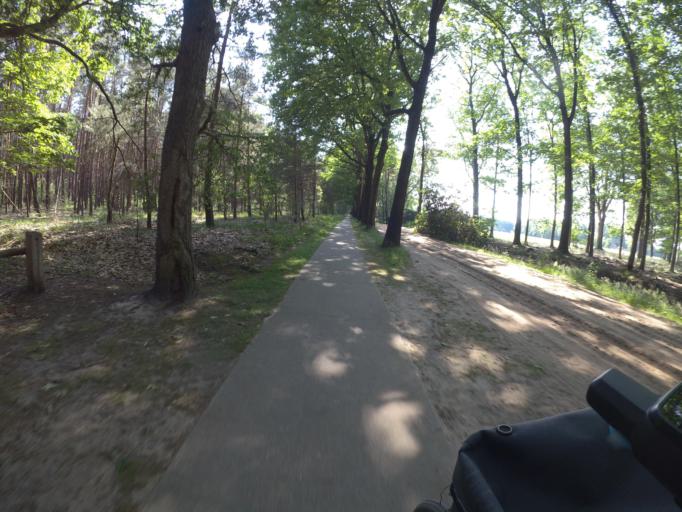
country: NL
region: Overijssel
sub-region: Gemeente Dalfsen
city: Dalfsen
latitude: 52.4858
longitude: 6.2745
